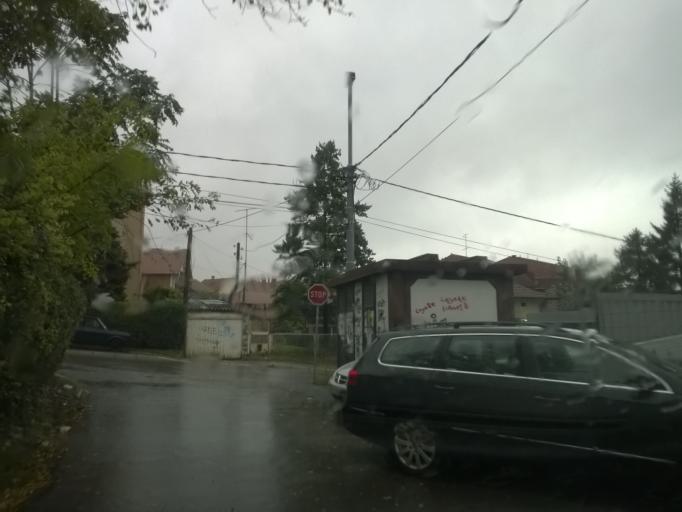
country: RS
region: Central Serbia
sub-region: Belgrade
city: Zvezdara
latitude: 44.7936
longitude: 20.5256
